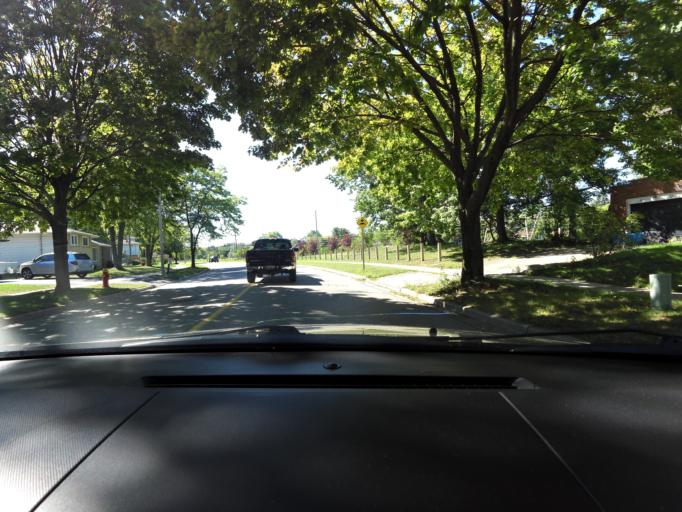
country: CA
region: Ontario
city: Burlington
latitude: 43.3577
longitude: -79.8171
